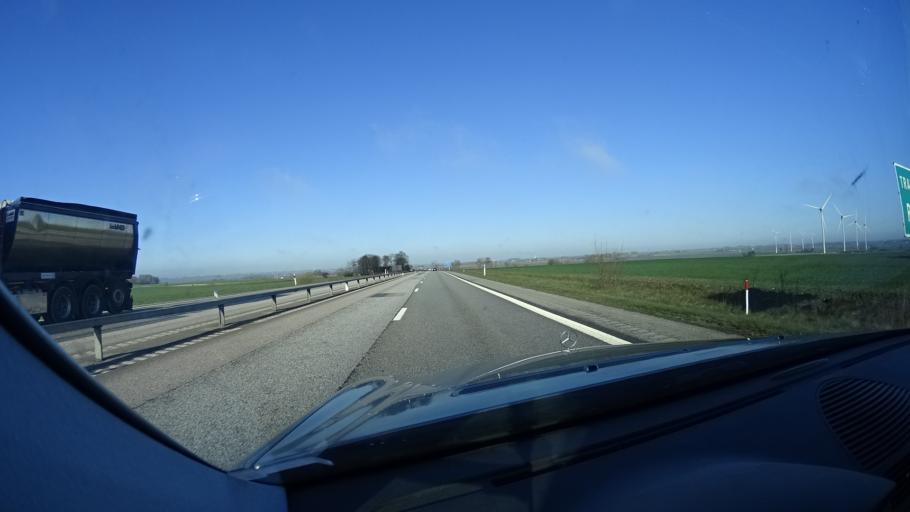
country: SE
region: Skane
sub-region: Eslovs Kommun
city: Eslov
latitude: 55.7780
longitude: 13.3790
